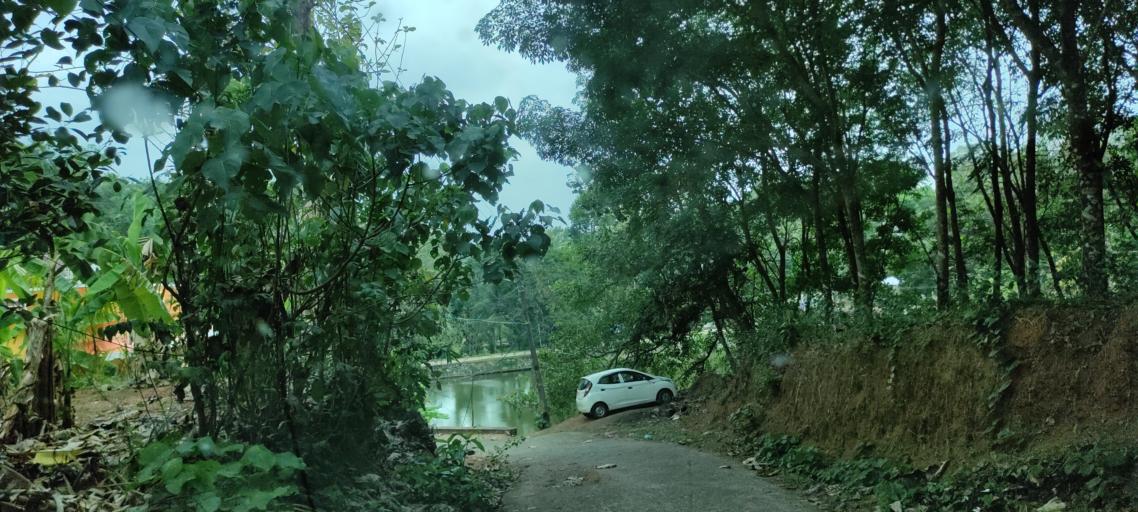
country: IN
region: Kerala
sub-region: Pattanamtitta
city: Adur
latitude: 9.1682
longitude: 76.7430
